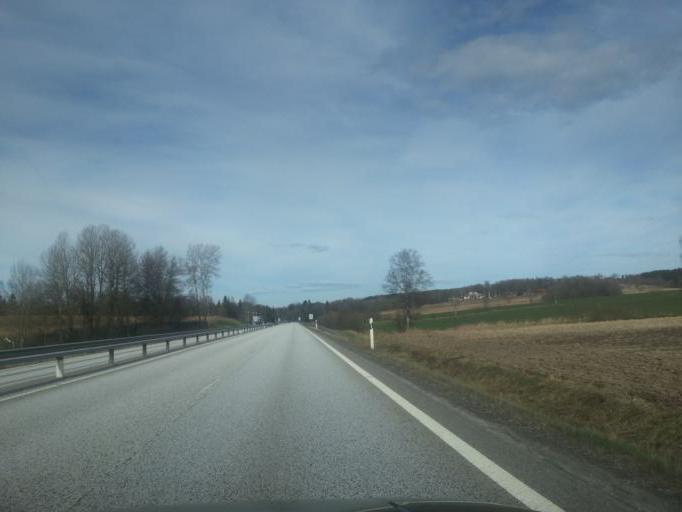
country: SE
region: Joenkoeping
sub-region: Jonkopings Kommun
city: Bankeryd
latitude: 57.8114
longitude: 14.0993
